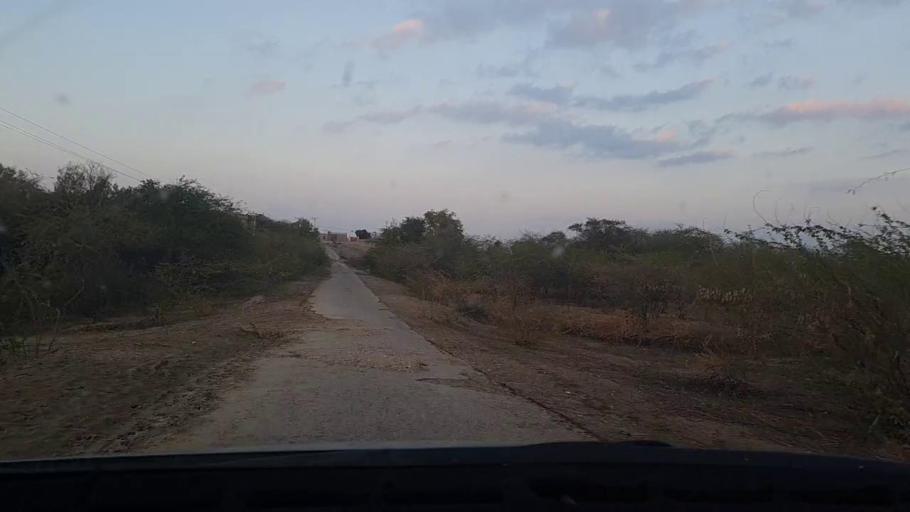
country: PK
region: Sindh
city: Tando Mittha Khan
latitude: 25.9657
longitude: 69.3474
